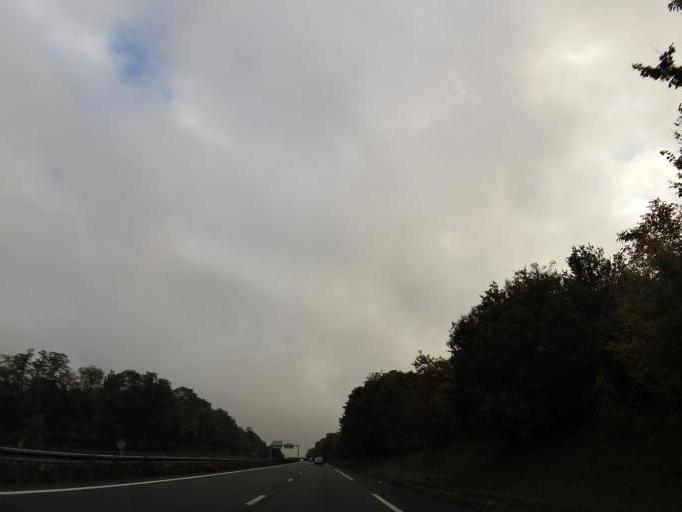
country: FR
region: Ile-de-France
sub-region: Departement de Seine-et-Marne
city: Bouleurs
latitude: 48.8896
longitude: 2.9019
